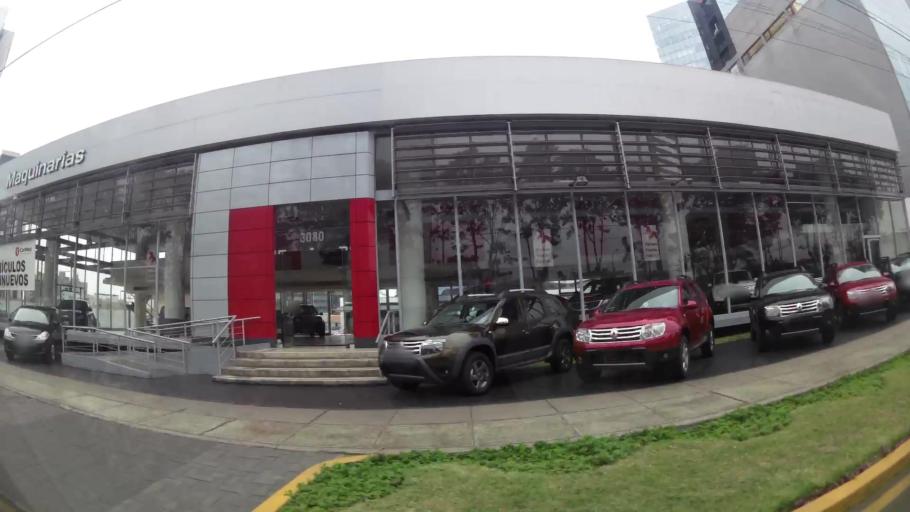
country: PE
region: Lima
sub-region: Lima
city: San Luis
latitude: -12.0938
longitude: -77.0222
